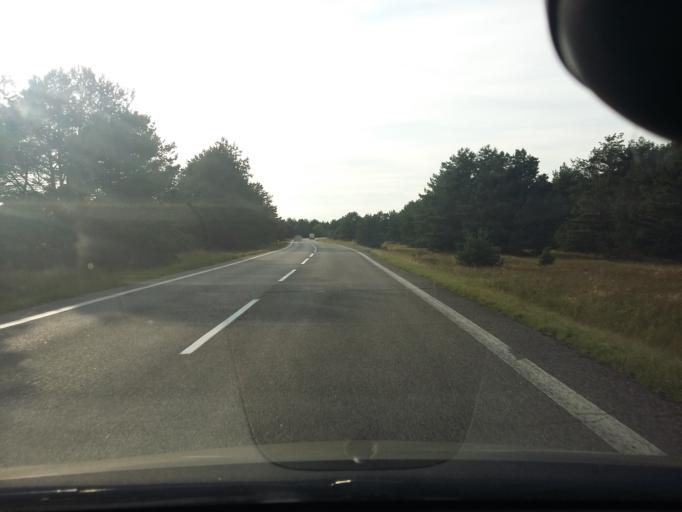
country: SK
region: Bratislavsky
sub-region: Okres Malacky
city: Malacky
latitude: 48.4069
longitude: 17.0773
